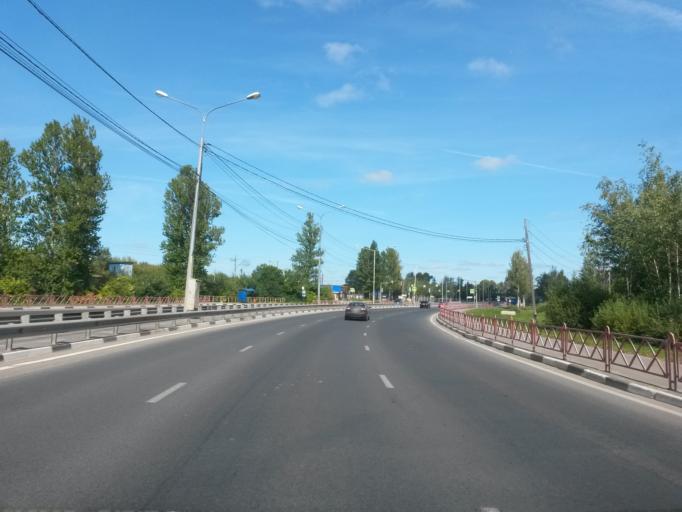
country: RU
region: Jaroslavl
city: Yaroslavl
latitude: 57.5937
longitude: 39.8939
